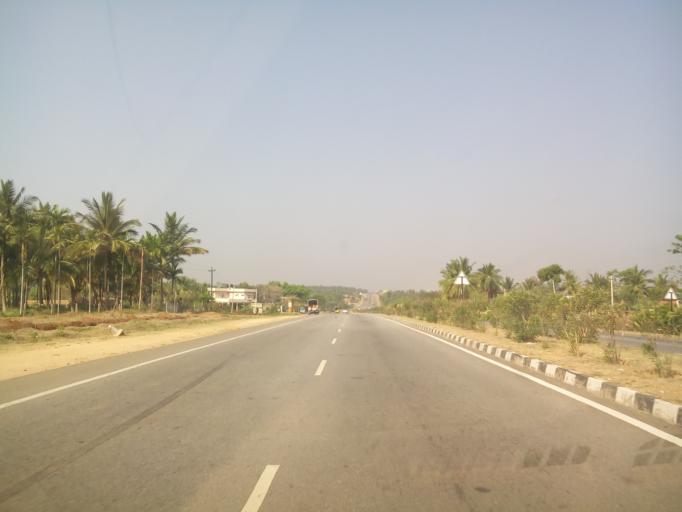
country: IN
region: Karnataka
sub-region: Tumkur
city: Kunigal
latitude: 13.0409
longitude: 77.1103
